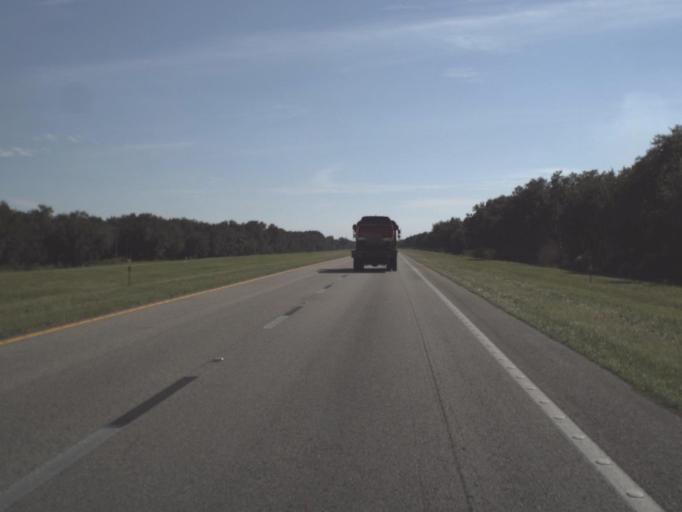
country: US
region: Florida
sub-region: Hendry County
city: Port LaBelle
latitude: 26.9660
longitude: -81.3167
